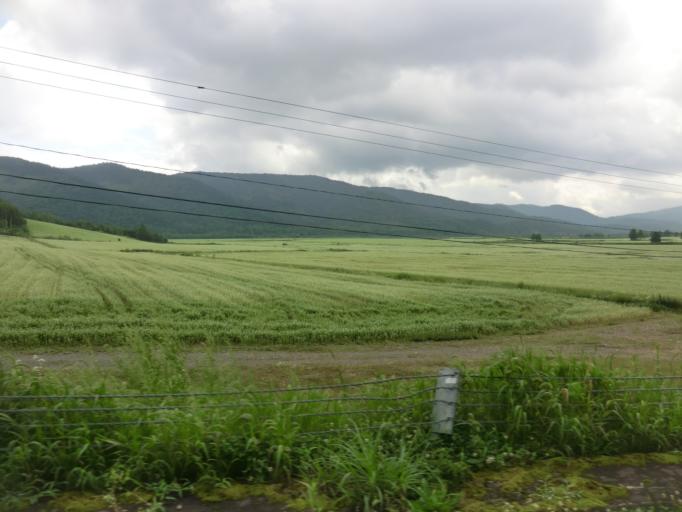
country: JP
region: Hokkaido
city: Nayoro
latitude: 44.1593
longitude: 142.1473
